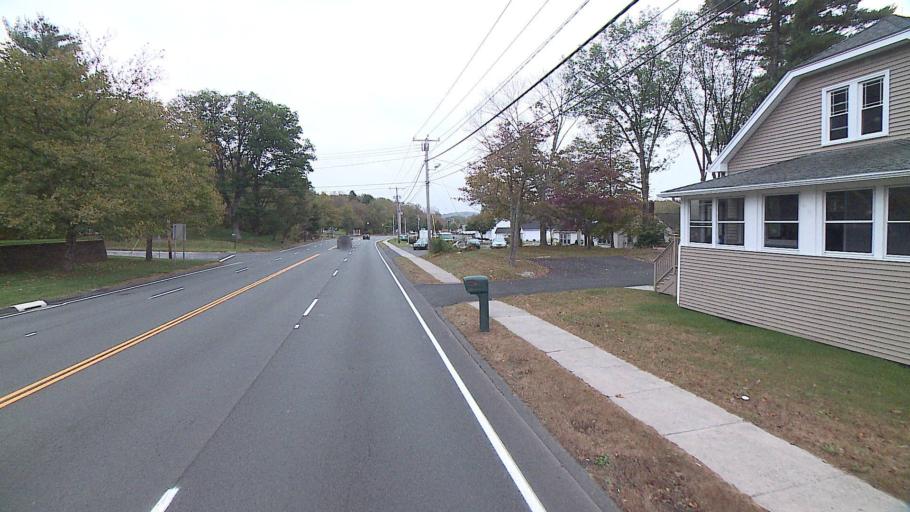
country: US
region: Connecticut
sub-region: Hartford County
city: Canton Valley
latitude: 41.8300
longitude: -72.9036
